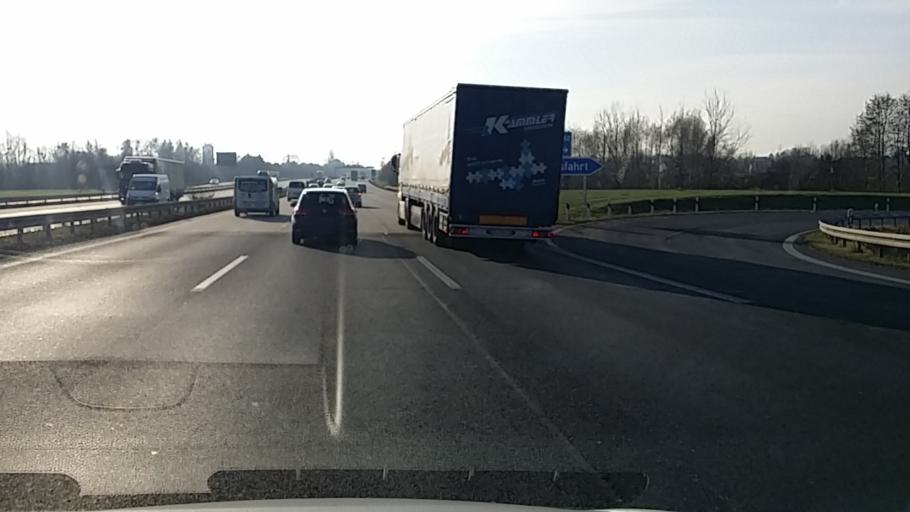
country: DE
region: Saxony
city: Albertstadt
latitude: 51.1235
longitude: 13.7470
